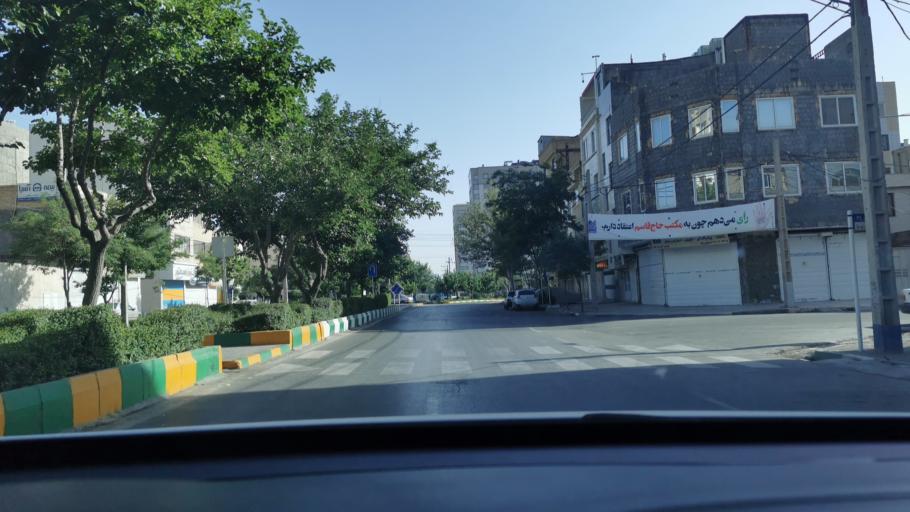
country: IR
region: Razavi Khorasan
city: Mashhad
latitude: 36.3397
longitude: 59.5138
